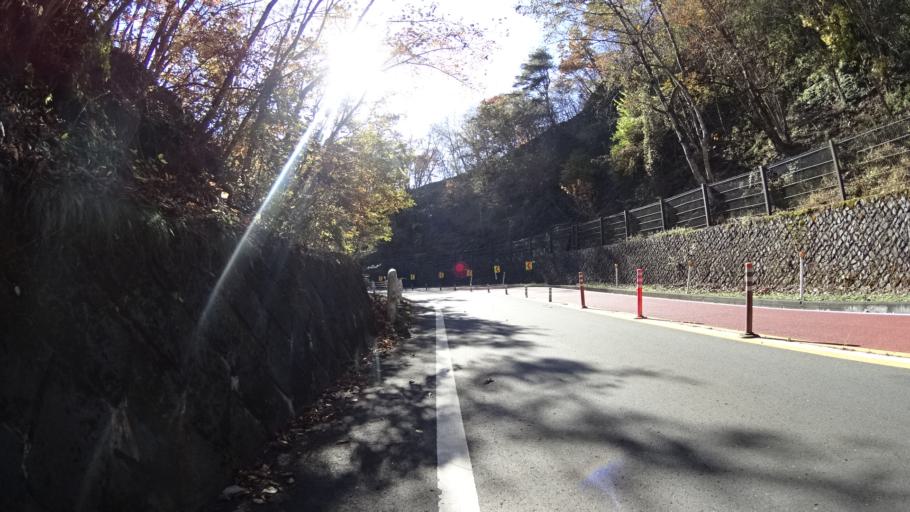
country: JP
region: Yamanashi
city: Uenohara
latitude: 35.7506
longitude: 139.0402
